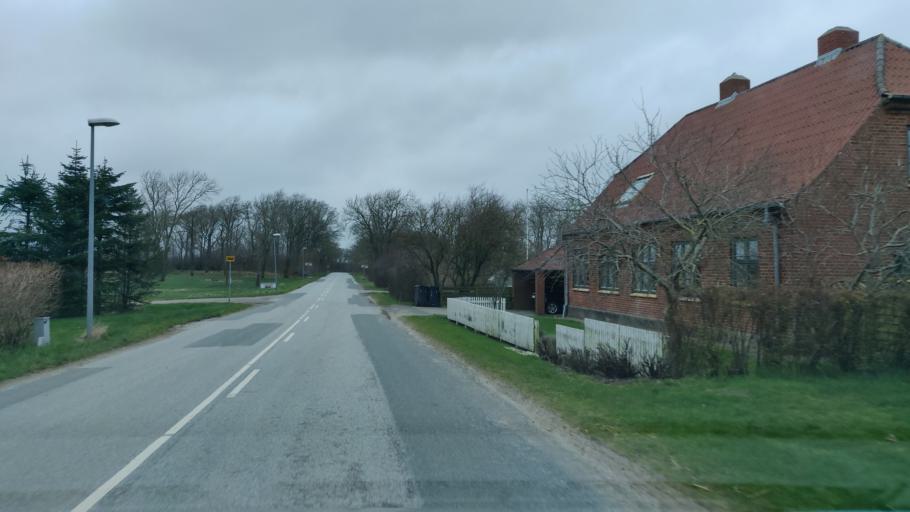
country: DK
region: Central Jutland
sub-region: Skive Kommune
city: Hojslev
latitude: 56.5552
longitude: 9.2477
